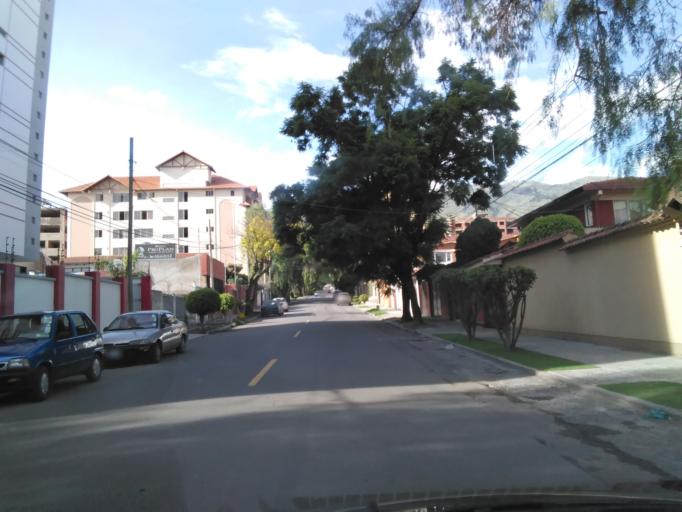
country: BO
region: Cochabamba
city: Cochabamba
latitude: -17.3727
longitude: -66.1466
